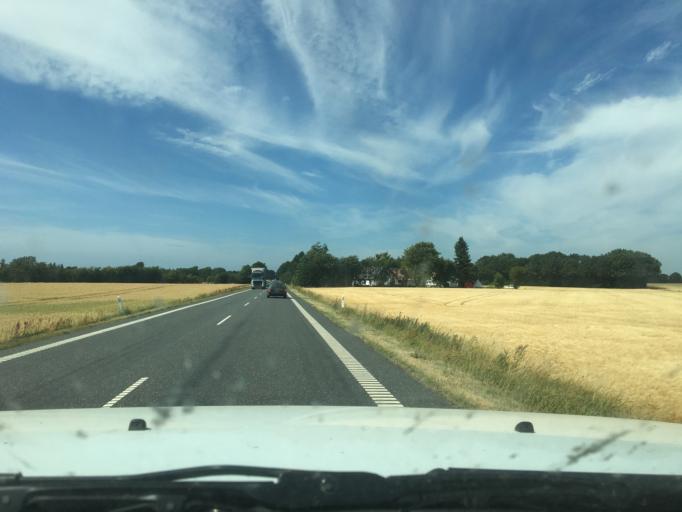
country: DK
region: Central Jutland
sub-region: Viborg Kommune
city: Viborg
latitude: 56.5961
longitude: 9.3628
